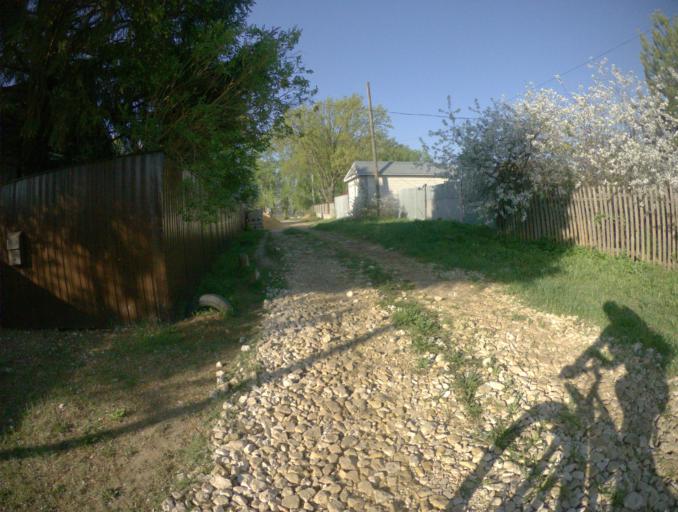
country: RU
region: Vladimir
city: Vyazniki
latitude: 56.2356
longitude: 42.1786
